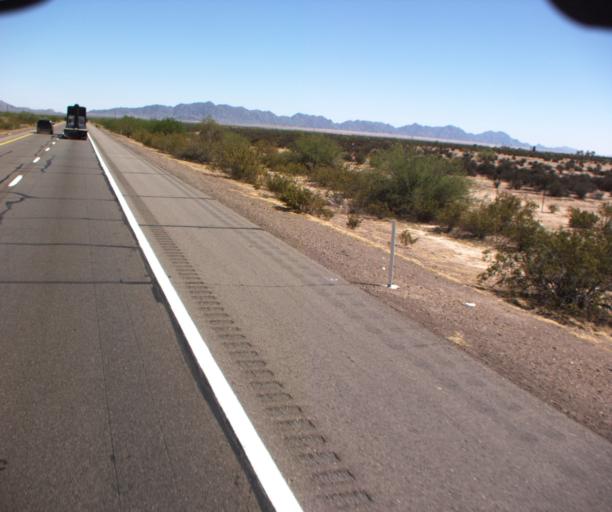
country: US
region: Arizona
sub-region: Yuma County
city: Wellton
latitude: 32.7015
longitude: -113.9000
